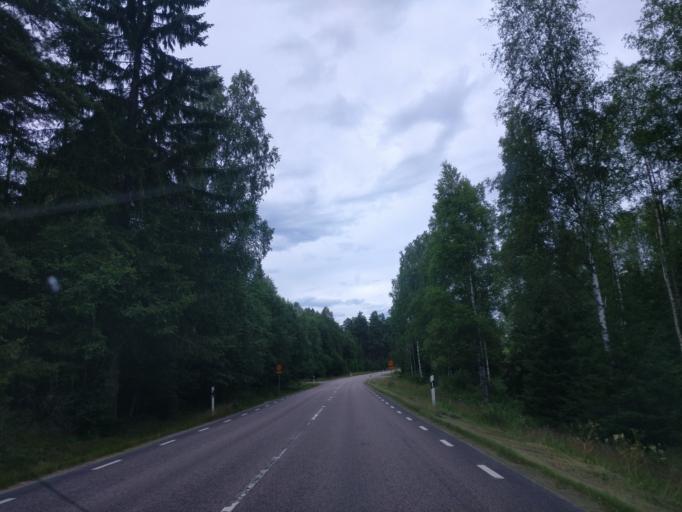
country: SE
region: Vaermland
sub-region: Hagfors Kommun
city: Ekshaerad
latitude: 60.1668
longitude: 13.4782
